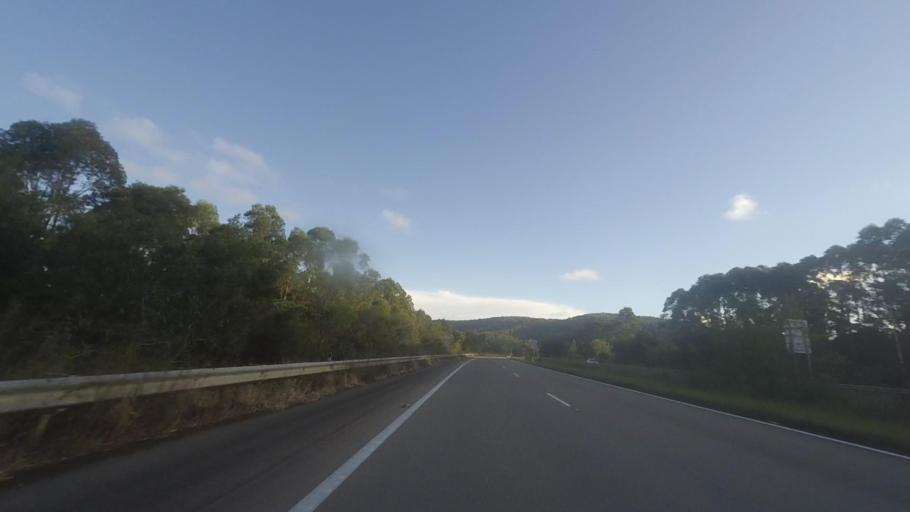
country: AU
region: New South Wales
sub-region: Great Lakes
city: Nabiac
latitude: -32.2646
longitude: 152.3281
